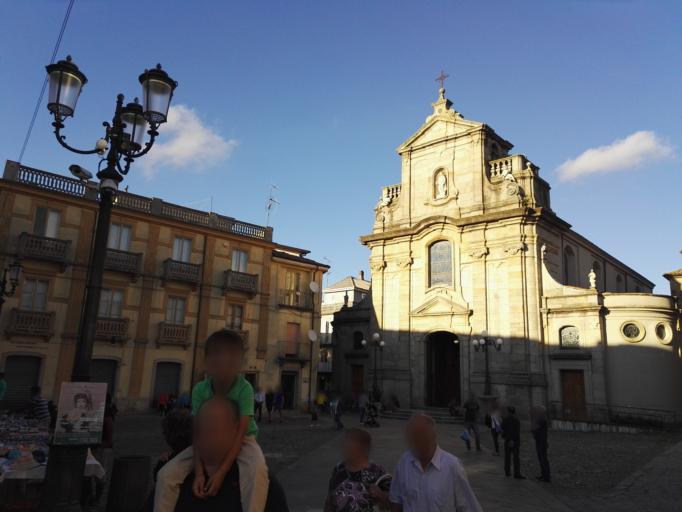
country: IT
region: Calabria
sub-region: Provincia di Vibo-Valentia
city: Serra San Bruno
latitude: 38.5793
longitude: 16.3323
